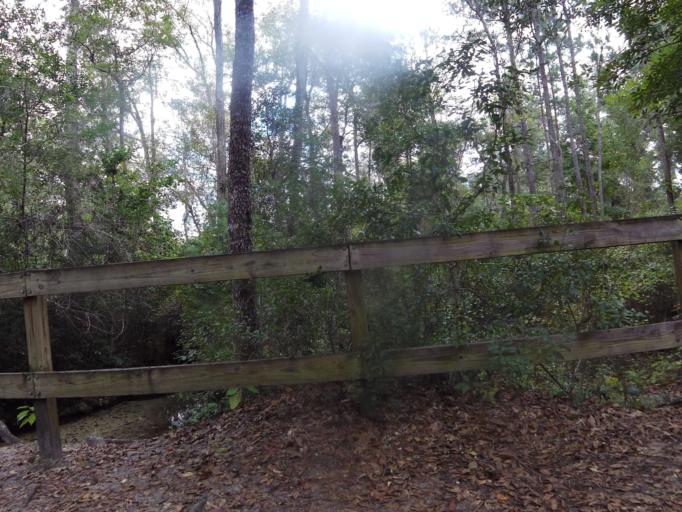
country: US
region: Florida
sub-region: Clay County
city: Keystone Heights
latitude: 29.8322
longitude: -81.9461
